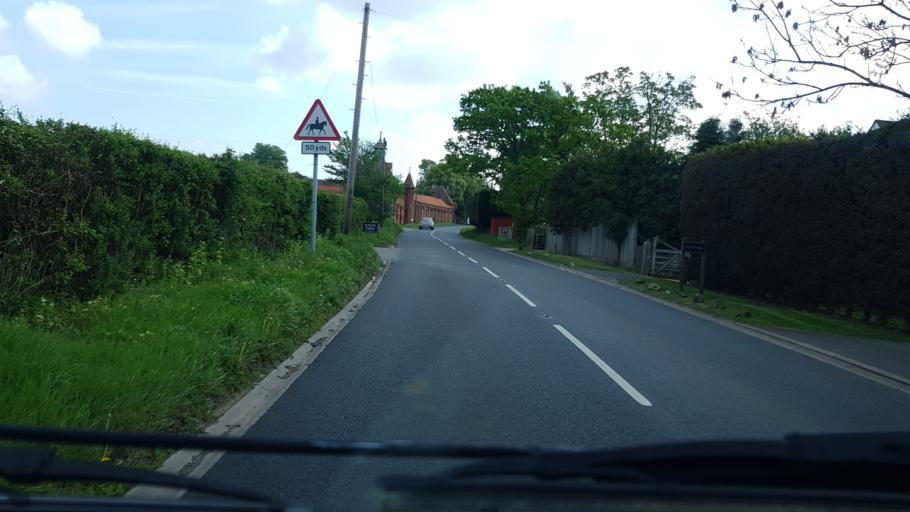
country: GB
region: England
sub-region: Surrey
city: Leatherhead
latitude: 51.3166
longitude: -0.3658
